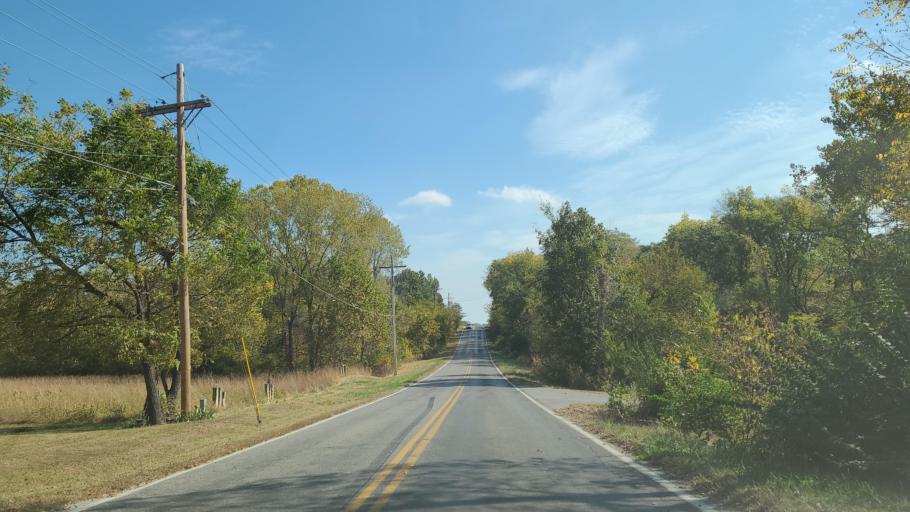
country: US
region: Kansas
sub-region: Douglas County
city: Lawrence
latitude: 38.9570
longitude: -95.2073
